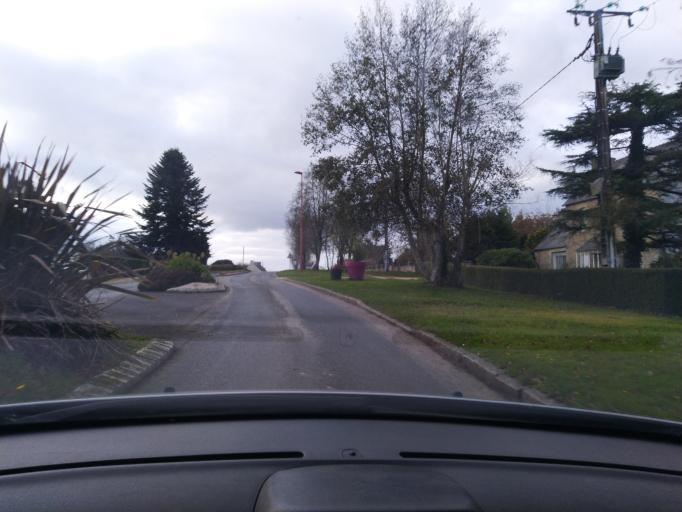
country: FR
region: Brittany
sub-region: Departement du Finistere
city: Guerlesquin
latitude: 48.5658
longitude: -3.5367
